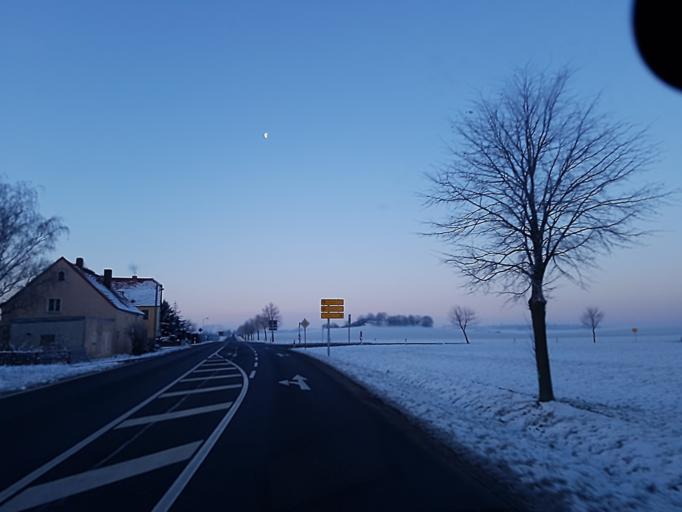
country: DE
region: Saxony
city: Oschatz
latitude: 51.3000
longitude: 13.1624
